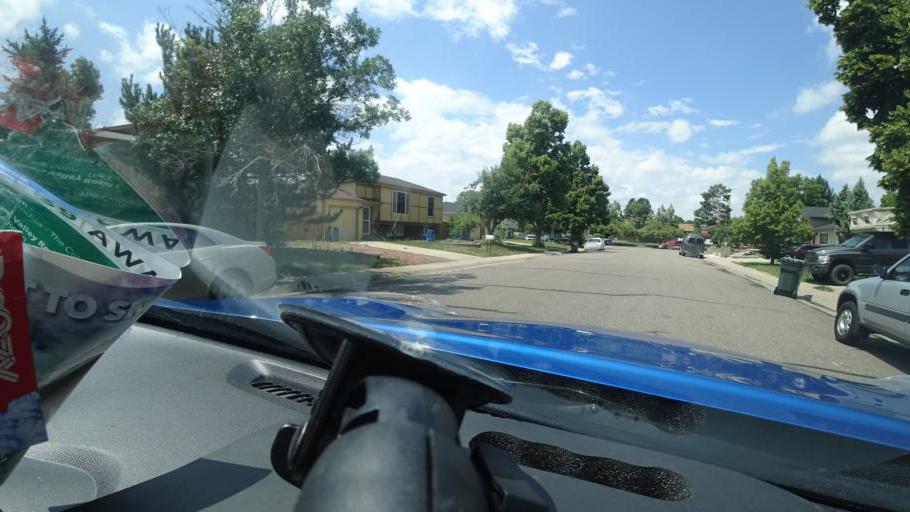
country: US
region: Colorado
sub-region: Adams County
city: Aurora
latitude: 39.7105
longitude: -104.8566
